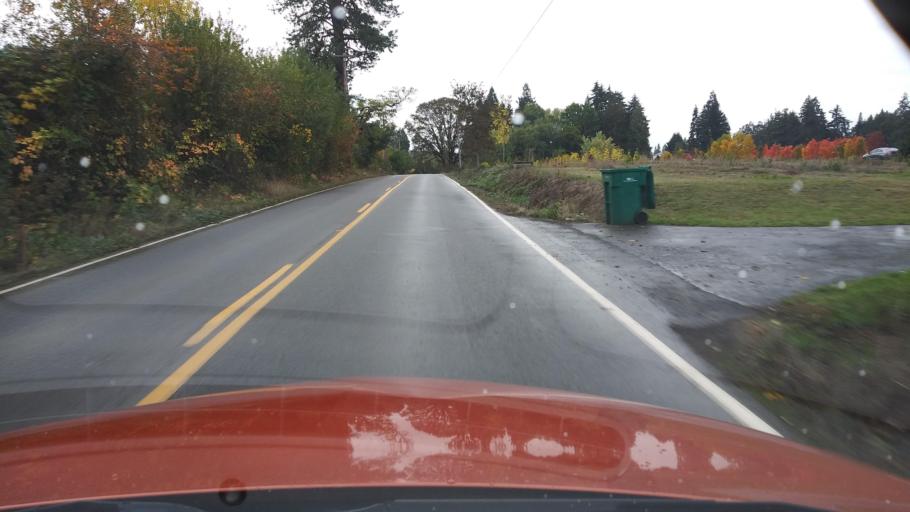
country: US
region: Oregon
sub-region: Washington County
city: Forest Grove
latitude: 45.5323
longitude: -123.0871
